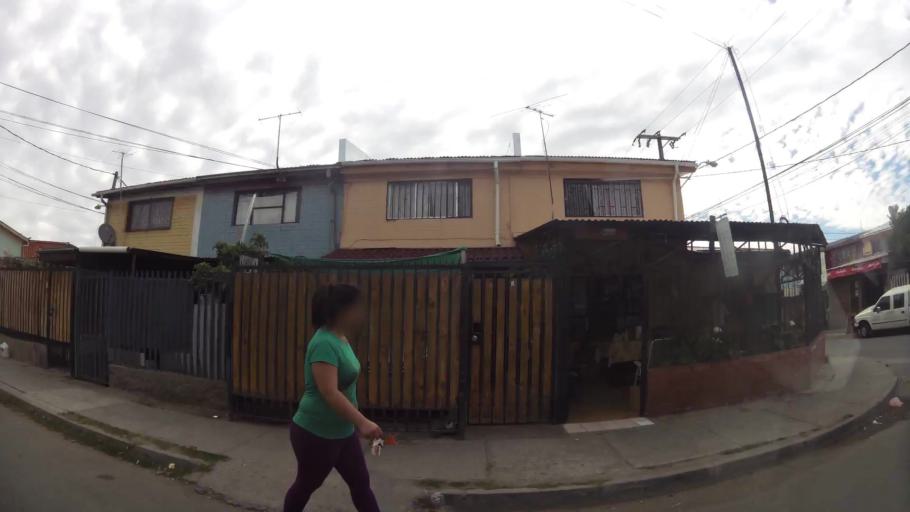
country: CL
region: Santiago Metropolitan
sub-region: Provincia de Santiago
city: La Pintana
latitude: -33.6143
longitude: -70.6211
